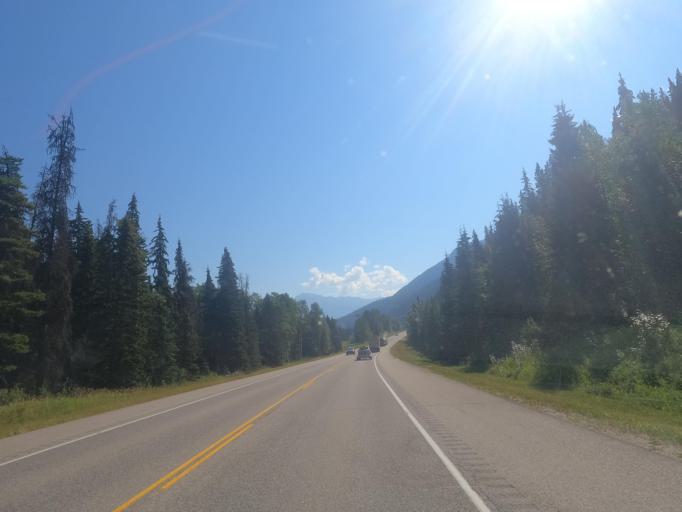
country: CA
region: Alberta
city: Jasper Park Lodge
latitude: 52.8601
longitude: -118.1766
